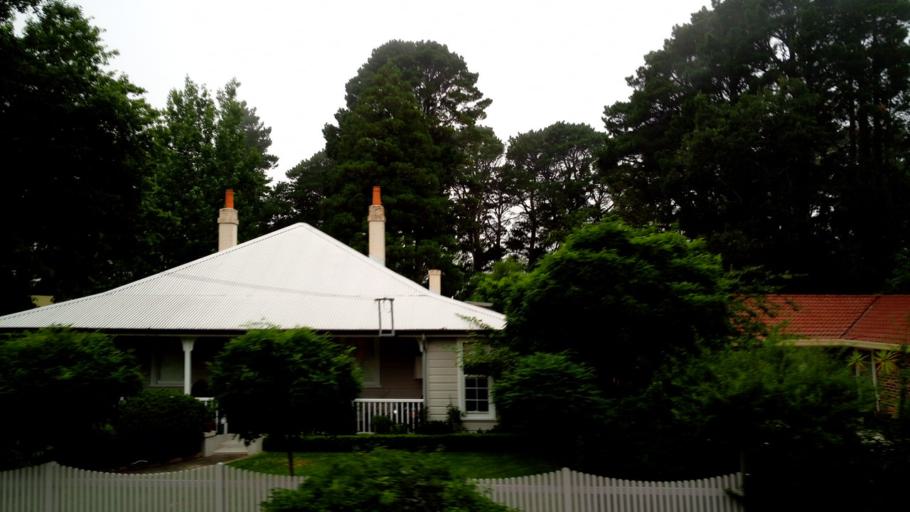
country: AU
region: New South Wales
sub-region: Blue Mountains Municipality
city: Leura
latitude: -33.7212
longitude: 150.3288
